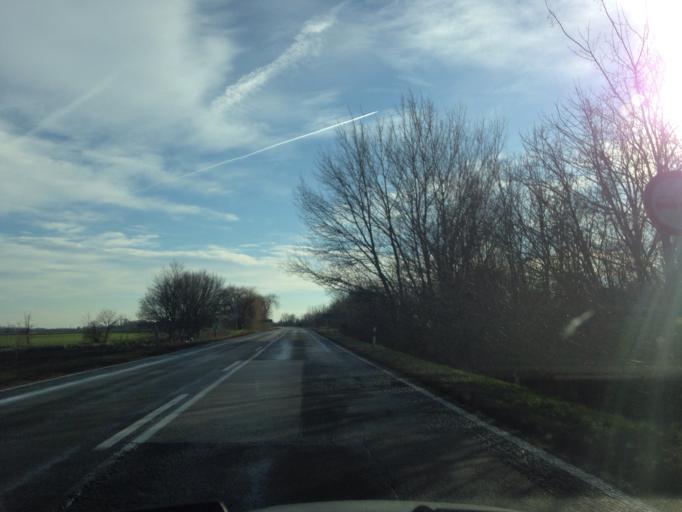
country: HU
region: Gyor-Moson-Sopron
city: Lebeny
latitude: 47.7783
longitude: 17.4177
